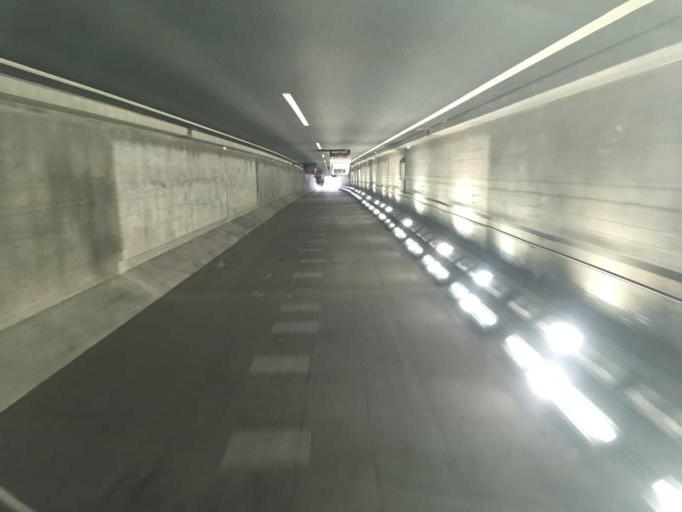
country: JP
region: Kanagawa
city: Zama
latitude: 35.5160
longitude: 139.3597
